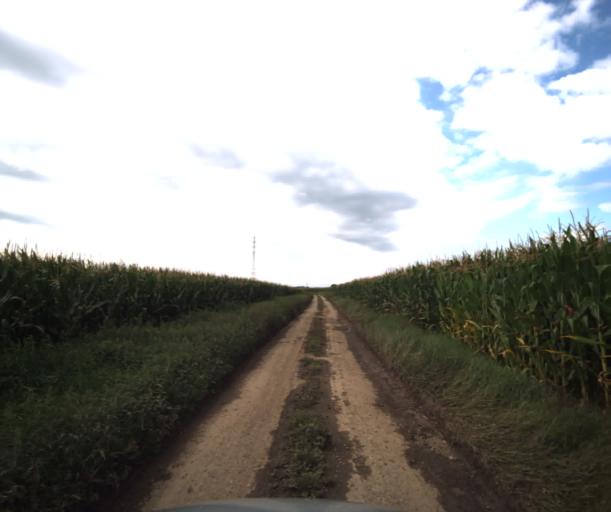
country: FR
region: Midi-Pyrenees
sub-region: Departement de la Haute-Garonne
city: Longages
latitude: 43.3834
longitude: 1.2324
